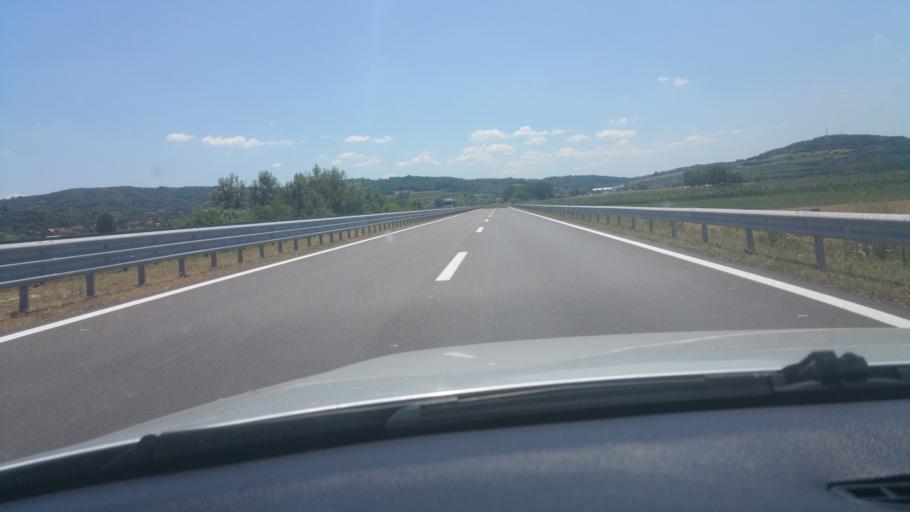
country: RS
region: Central Serbia
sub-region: Sumadijski Okrug
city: Batocina
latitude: 44.1324
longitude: 21.0198
